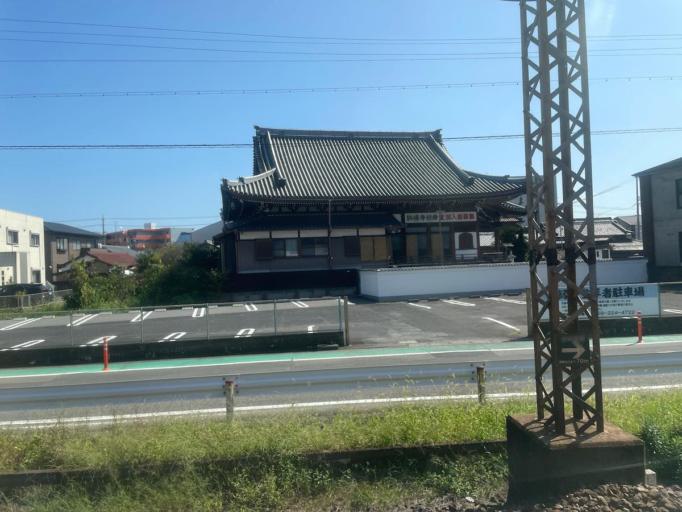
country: JP
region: Mie
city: Tsu-shi
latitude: 34.7420
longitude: 136.5135
